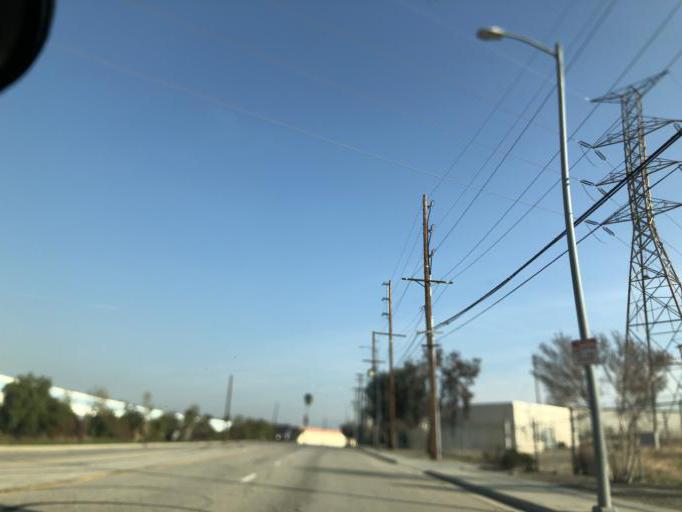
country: US
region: California
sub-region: Los Angeles County
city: San Fernando
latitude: 34.3131
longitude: -118.4795
